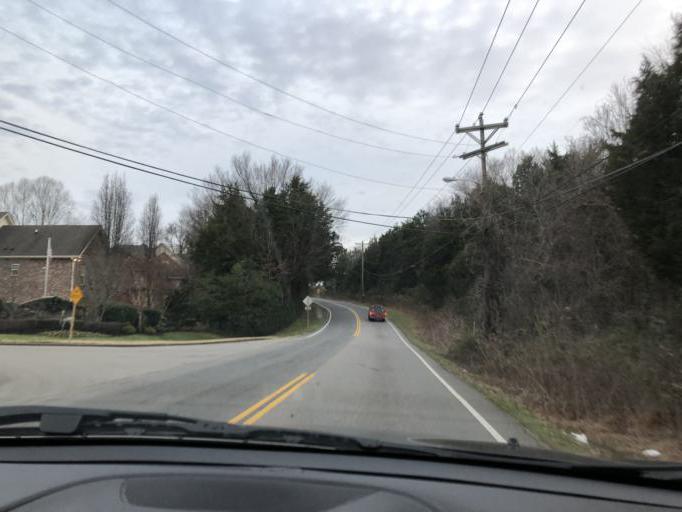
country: US
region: Tennessee
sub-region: Wilson County
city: Green Hill
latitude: 36.1992
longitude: -86.5924
